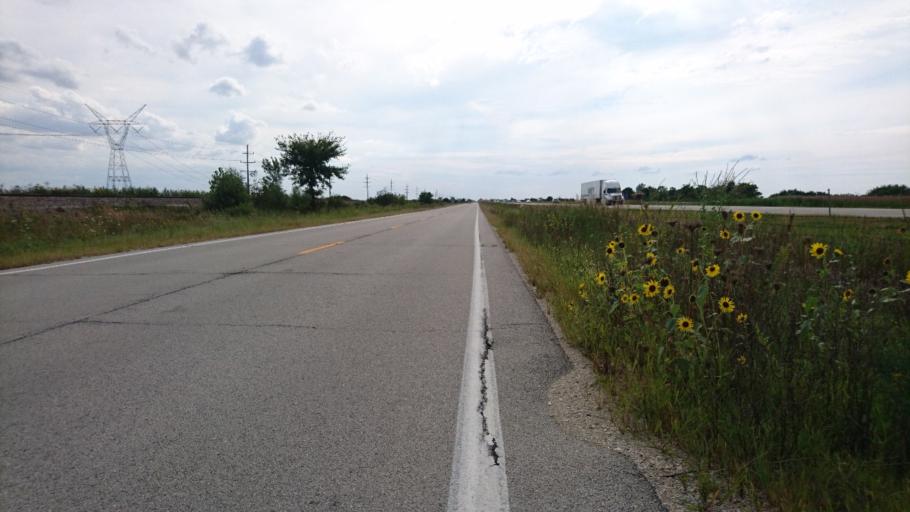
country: US
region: Illinois
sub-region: Livingston County
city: Dwight
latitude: 41.1333
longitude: -88.3774
